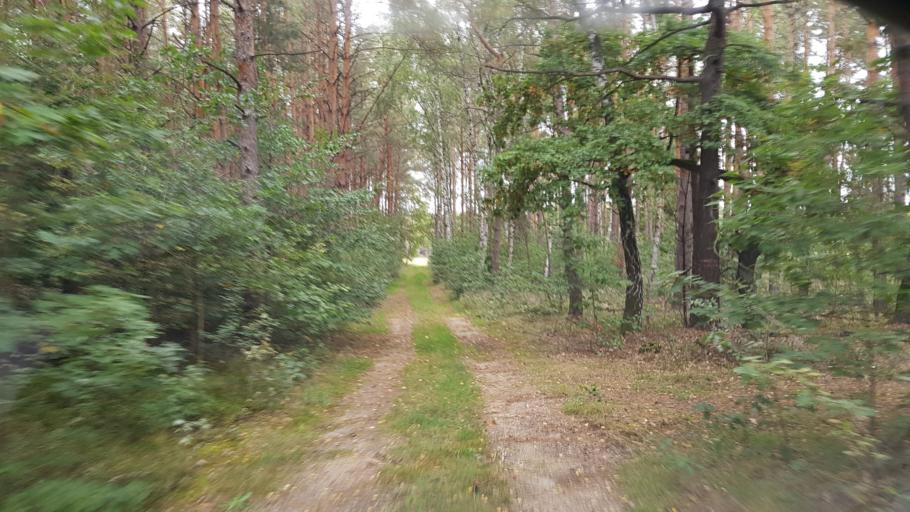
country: DE
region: Brandenburg
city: Finsterwalde
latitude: 51.5797
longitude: 13.6614
